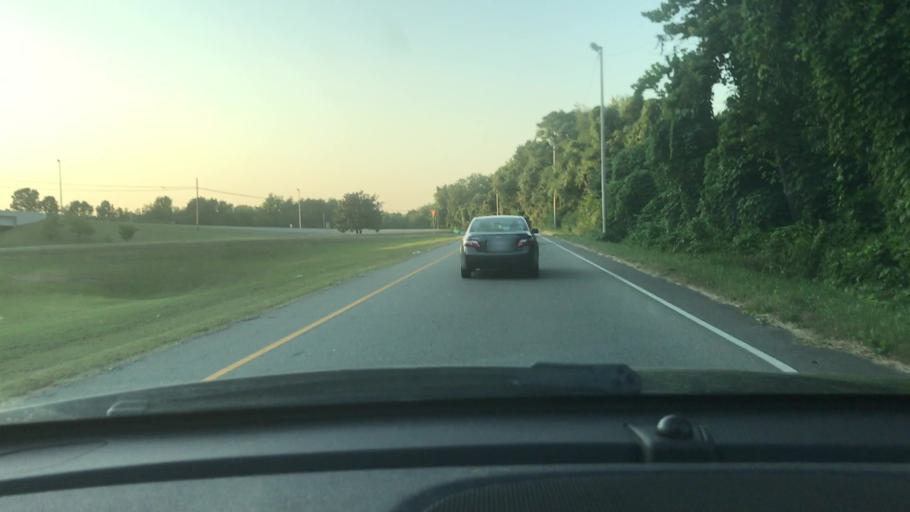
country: US
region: Tennessee
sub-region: Dickson County
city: Dickson
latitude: 36.0812
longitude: -87.3788
